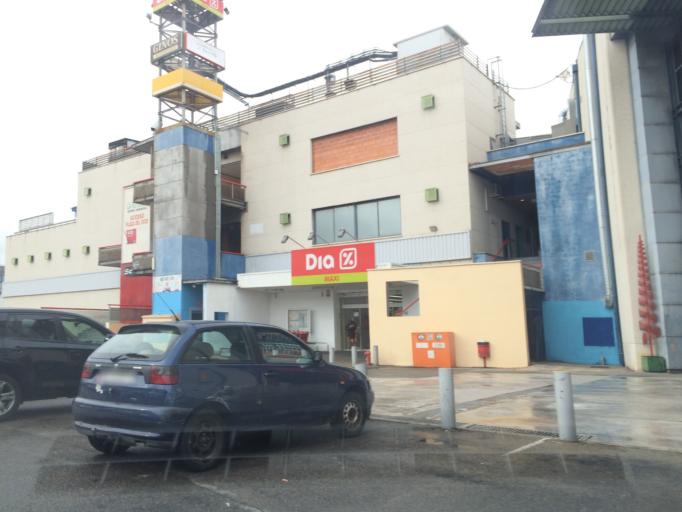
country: ES
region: Madrid
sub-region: Provincia de Madrid
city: Tres Cantos
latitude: 40.6052
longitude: -3.7170
